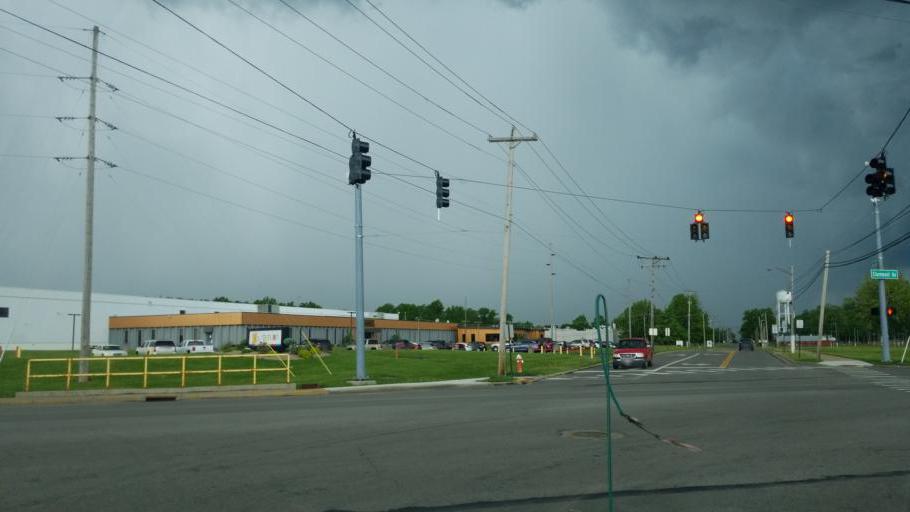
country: US
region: Ohio
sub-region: Ashland County
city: Ashland
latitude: 40.8469
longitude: -82.3491
